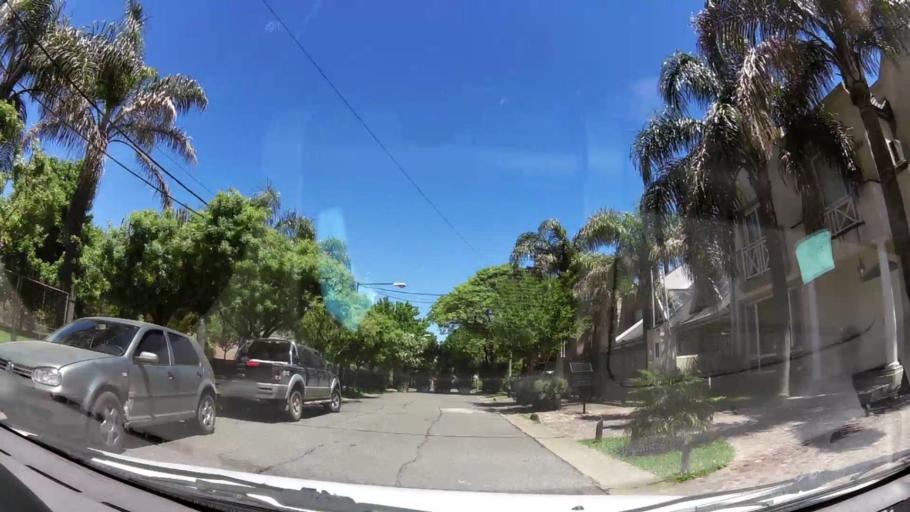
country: AR
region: Buenos Aires
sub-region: Partido de Vicente Lopez
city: Olivos
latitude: -34.5034
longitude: -58.5190
